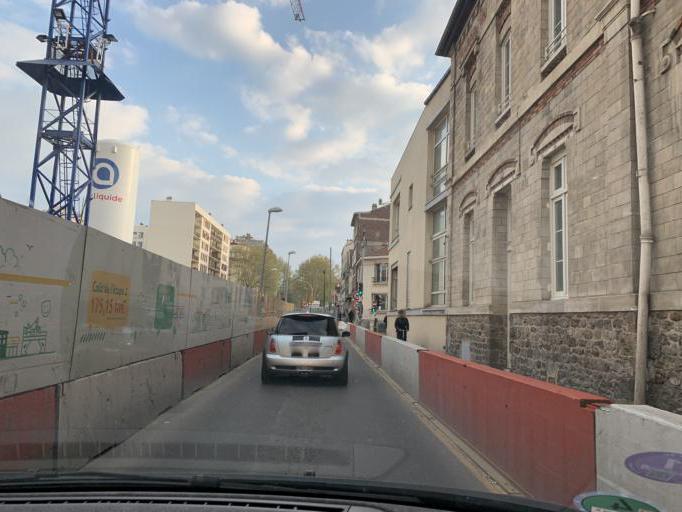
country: FR
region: Ile-de-France
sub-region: Departement de Seine-Saint-Denis
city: Aubervilliers
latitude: 48.9128
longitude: 2.3800
